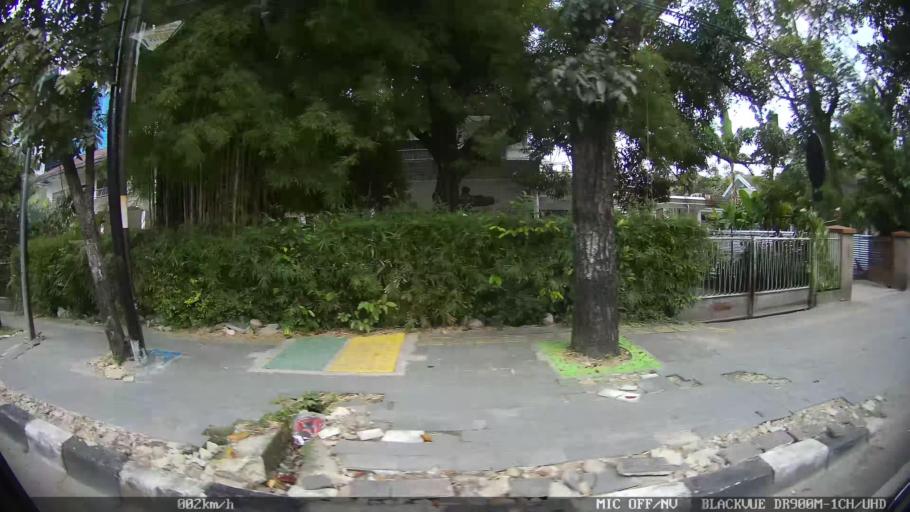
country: ID
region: North Sumatra
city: Medan
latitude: 3.5828
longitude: 98.6729
